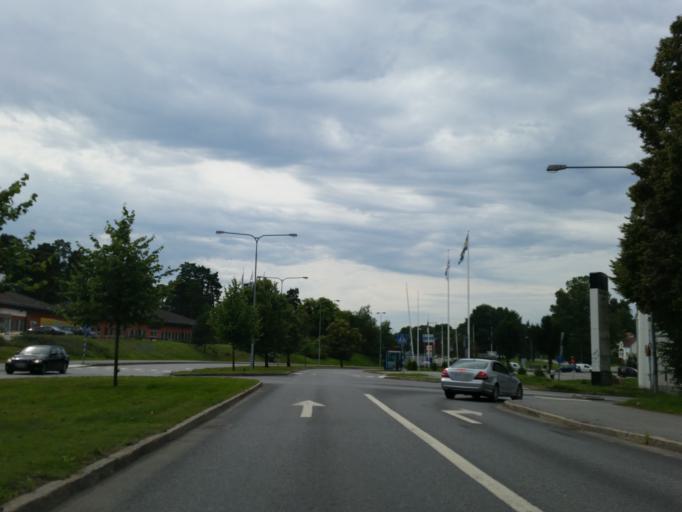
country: SE
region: Stockholm
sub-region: Sodertalje Kommun
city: Soedertaelje
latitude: 59.2056
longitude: 17.6463
